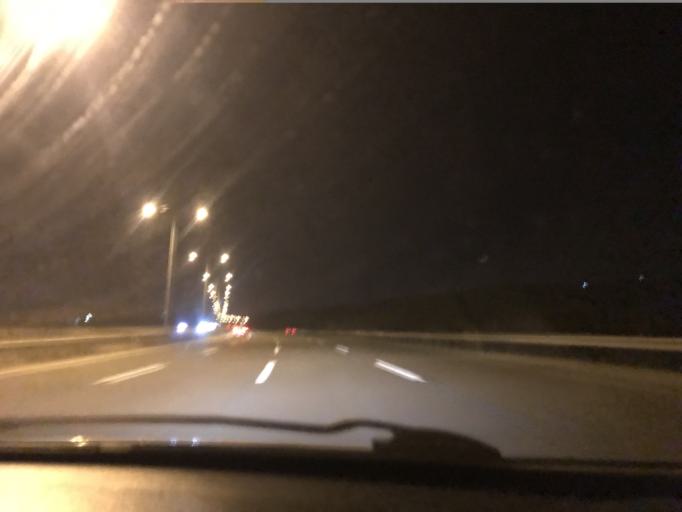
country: TR
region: Ankara
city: Etimesgut
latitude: 39.8818
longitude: 32.6160
